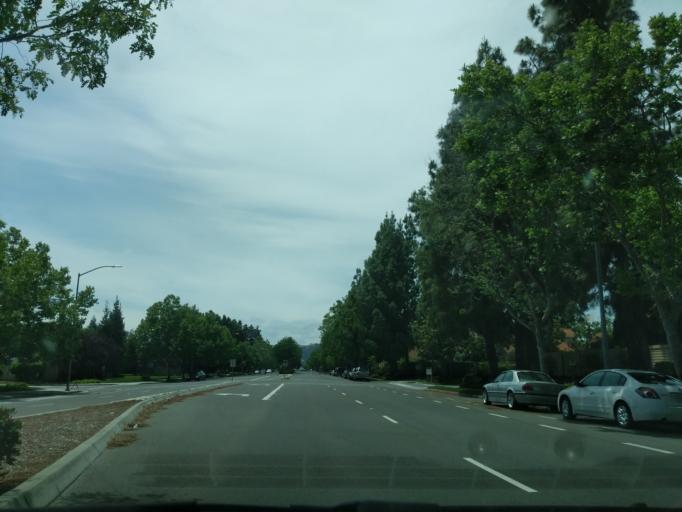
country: US
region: California
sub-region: Santa Clara County
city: Morgan Hill
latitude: 37.1376
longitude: -121.6180
